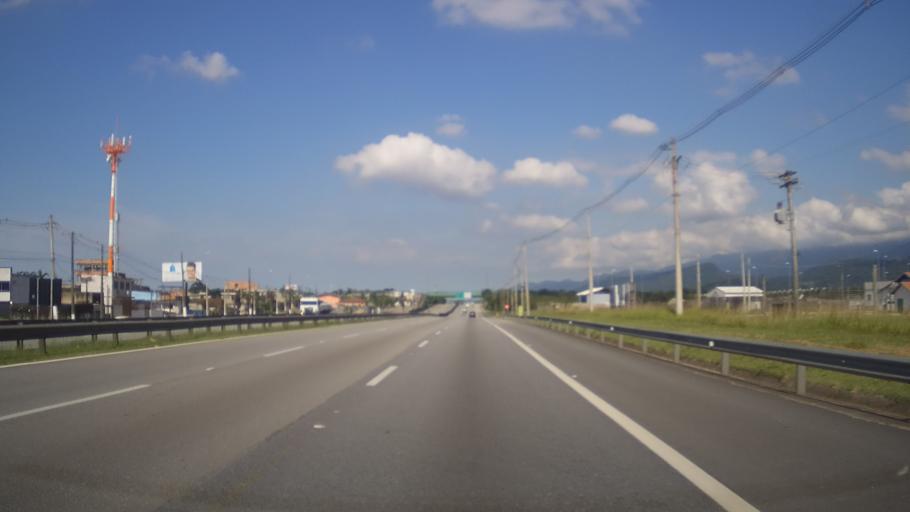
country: BR
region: Sao Paulo
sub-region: Praia Grande
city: Praia Grande
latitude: -23.9721
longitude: -46.4770
